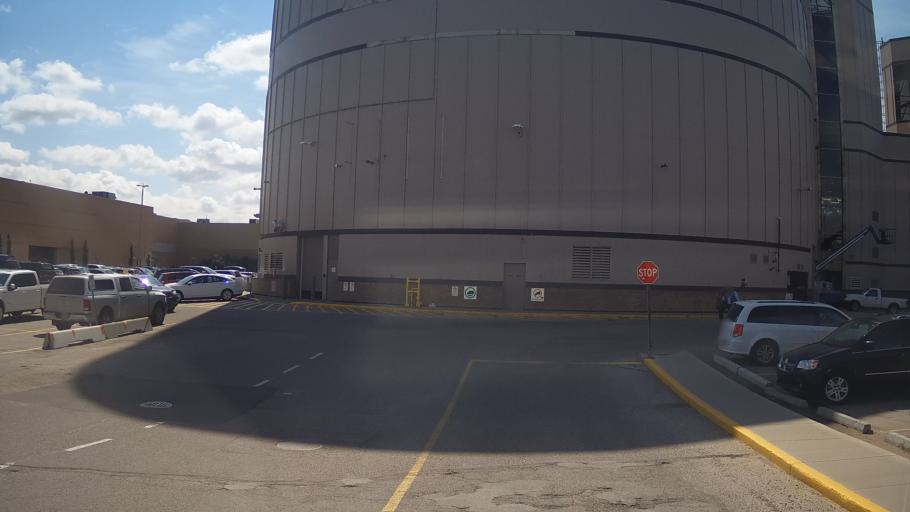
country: CA
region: Alberta
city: St. Albert
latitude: 53.5247
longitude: -113.6201
